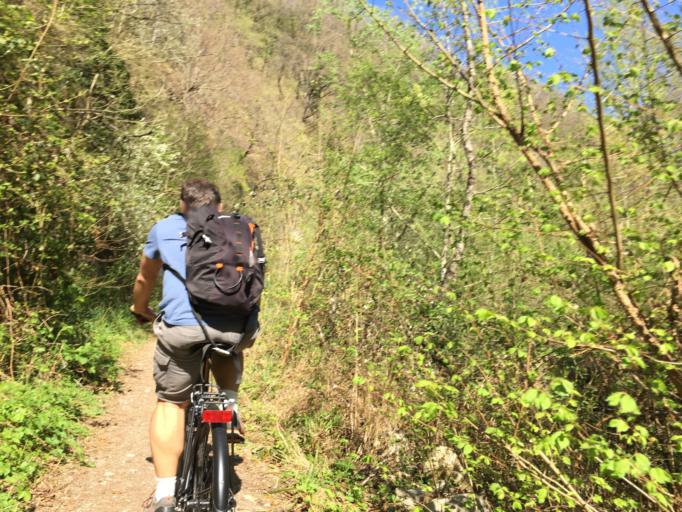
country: FR
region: Rhone-Alpes
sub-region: Departement de la Savoie
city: Barby
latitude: 45.5818
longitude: 5.9807
